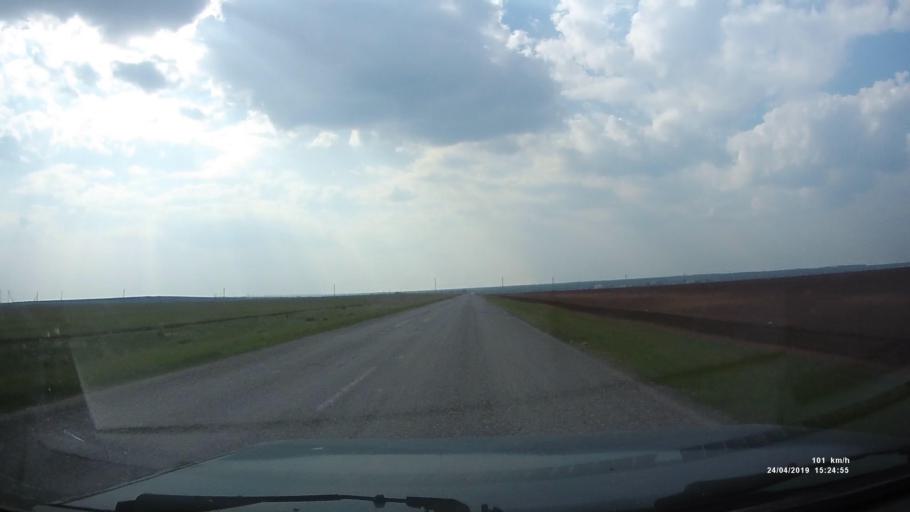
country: RU
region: Rostov
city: Remontnoye
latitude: 46.5500
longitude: 43.0587
